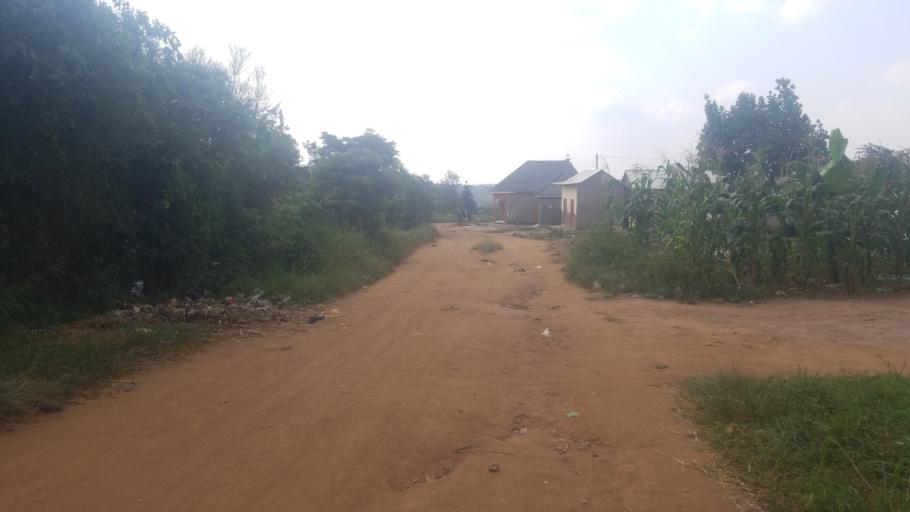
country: UG
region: Central Region
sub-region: Sembabule District
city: Sembabule
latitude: -0.0832
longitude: 31.4578
